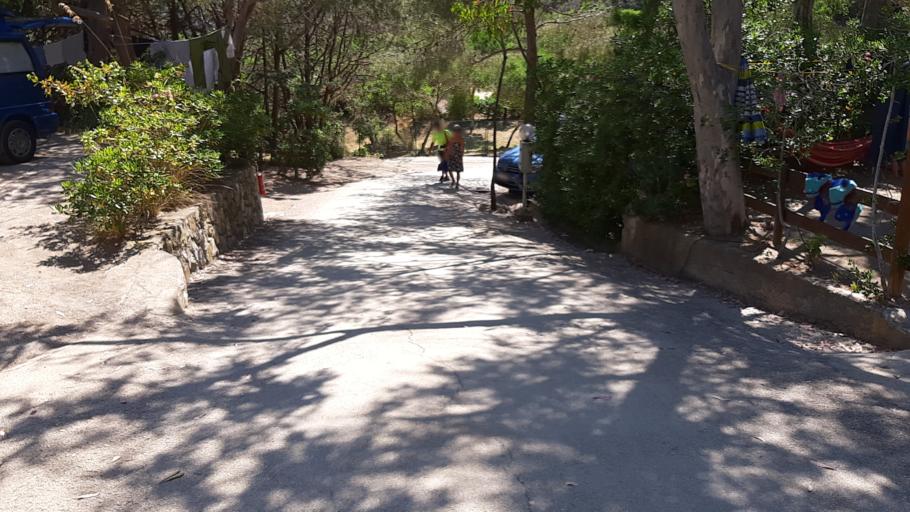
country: IT
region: Tuscany
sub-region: Provincia di Livorno
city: Portoferraio
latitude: 42.7581
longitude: 10.2966
